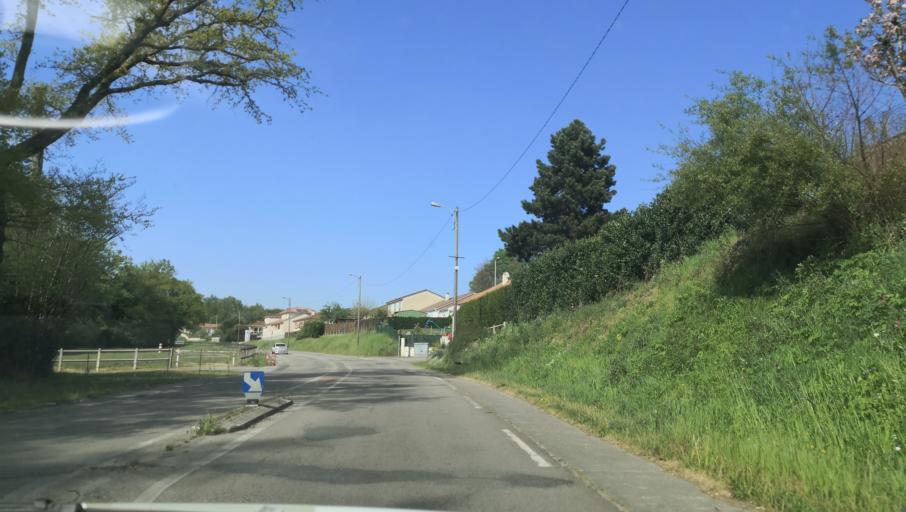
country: FR
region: Limousin
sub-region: Departement de la Haute-Vienne
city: Couzeix
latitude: 45.8621
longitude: 1.2586
